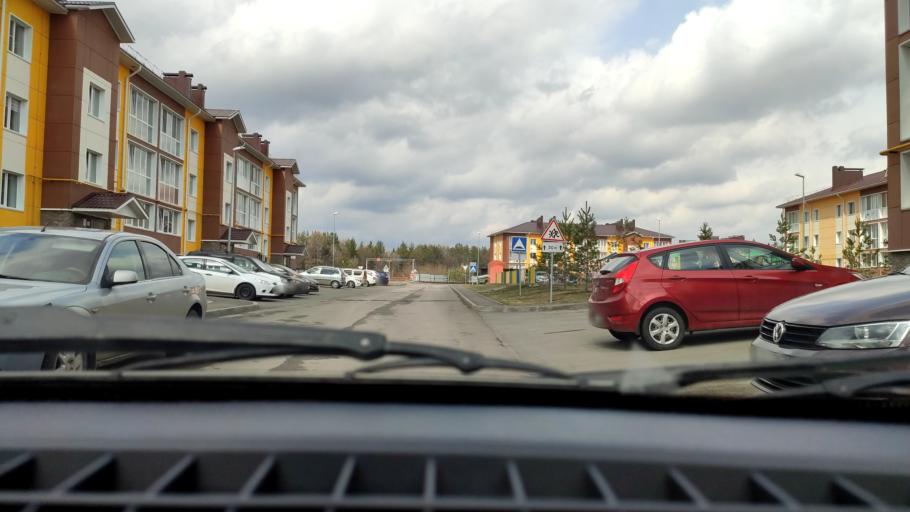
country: RU
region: Bashkortostan
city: Ufa
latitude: 54.5897
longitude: 55.9171
